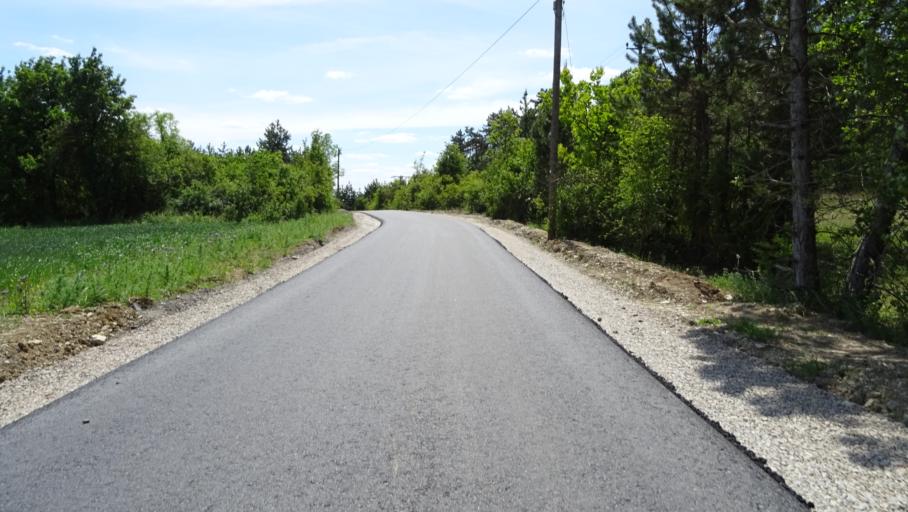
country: DE
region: Baden-Wuerttemberg
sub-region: Karlsruhe Region
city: Seckach
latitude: 49.4804
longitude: 9.3270
